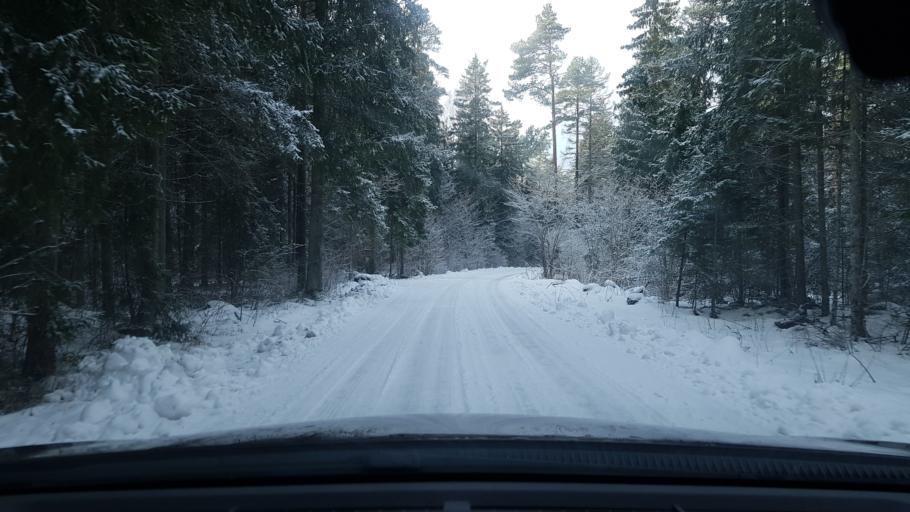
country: EE
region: Harju
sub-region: Keila linn
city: Keila
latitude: 59.2927
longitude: 24.2603
